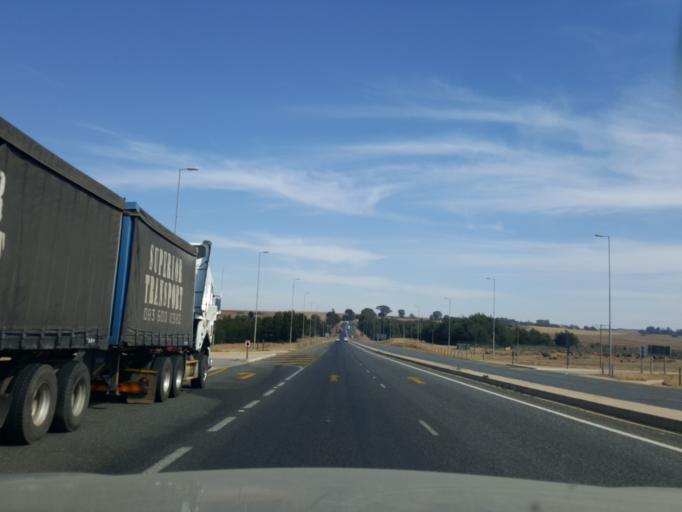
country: ZA
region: Mpumalanga
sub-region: Nkangala District Municipality
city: Belfast
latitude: -25.7295
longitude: 30.1336
